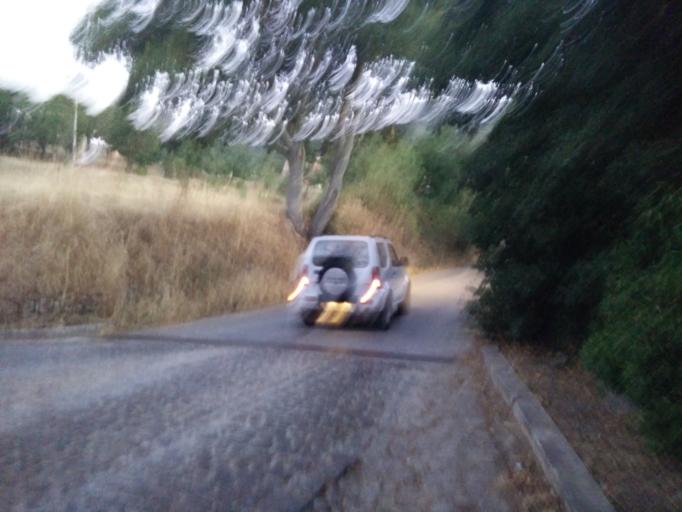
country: IT
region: Sicily
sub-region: Palermo
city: Castelbuono
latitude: 37.9258
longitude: 14.0873
